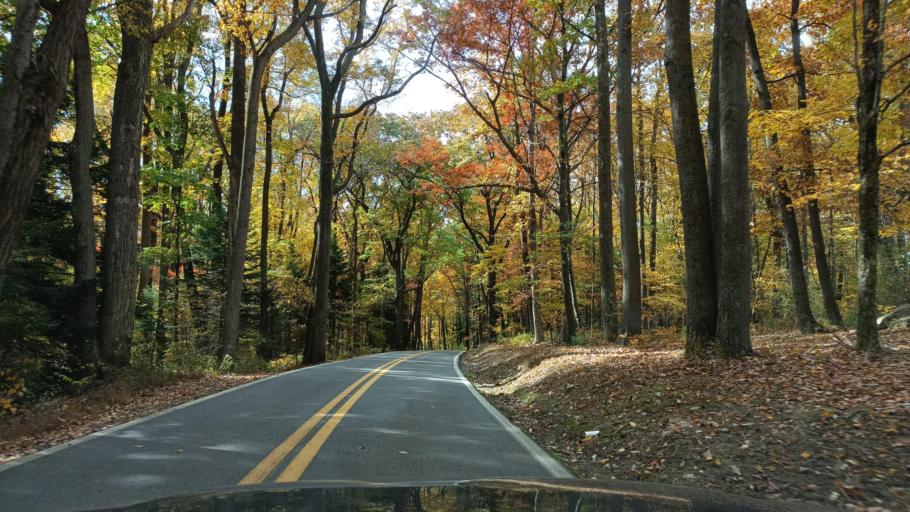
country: US
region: West Virginia
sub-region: Monongalia County
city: Cheat Lake
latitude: 39.6445
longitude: -79.7926
